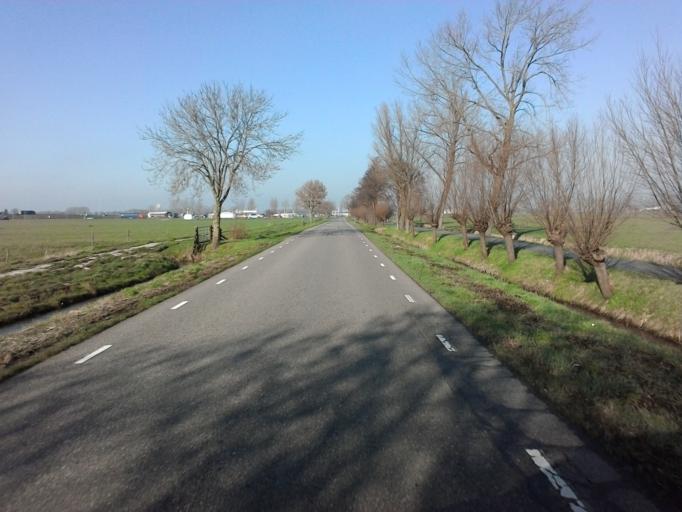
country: NL
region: South Holland
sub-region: Gemeente Gorinchem
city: Gorinchem
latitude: 51.8946
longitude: 4.9838
